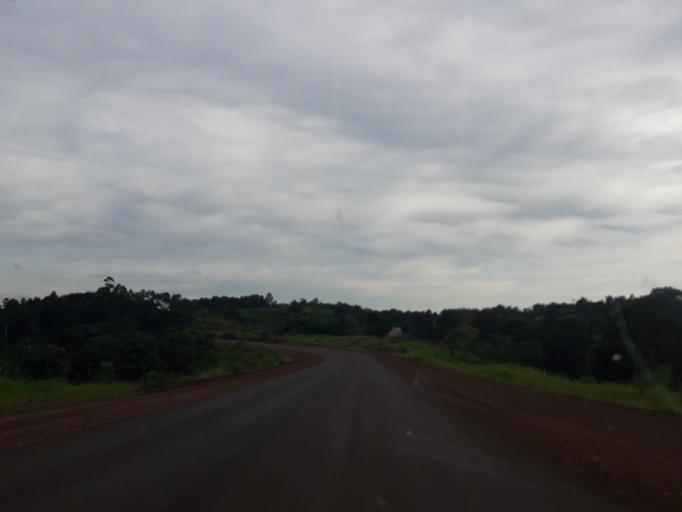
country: AR
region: Misiones
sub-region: Departamento de San Pedro
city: San Pedro
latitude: -26.5180
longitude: -53.9369
